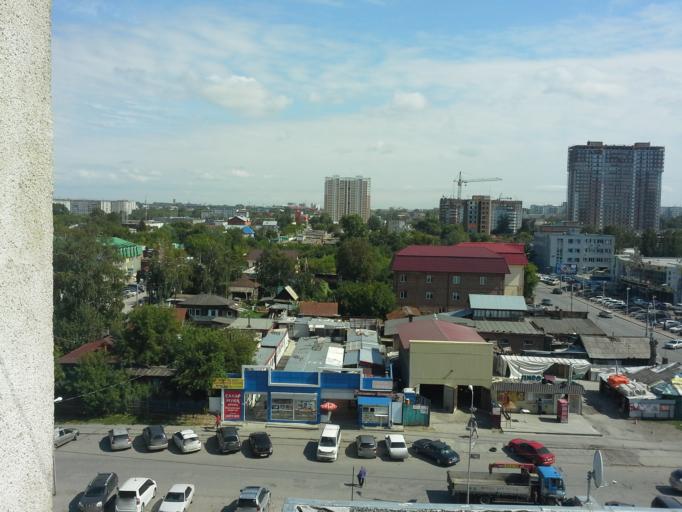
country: RU
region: Novosibirsk
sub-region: Novosibirskiy Rayon
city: Novosibirsk
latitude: 55.0500
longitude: 82.9270
